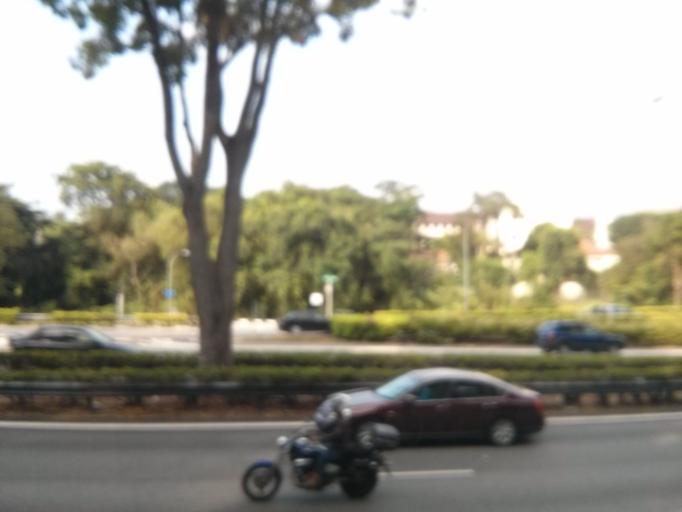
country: SG
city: Singapore
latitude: 1.2851
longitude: 103.7988
